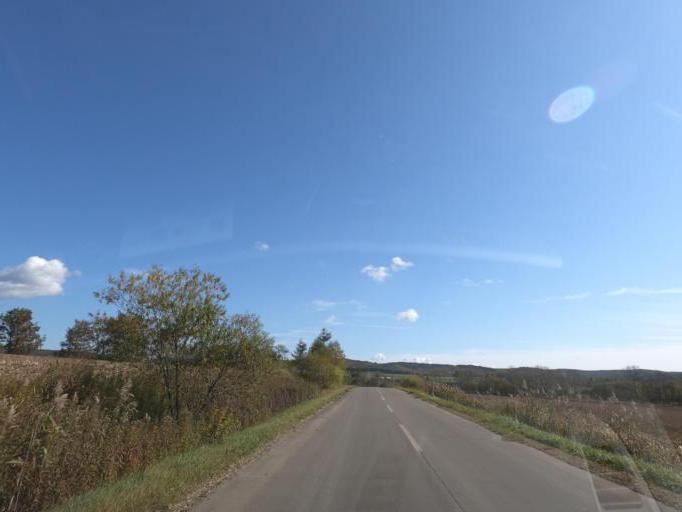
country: JP
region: Hokkaido
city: Otofuke
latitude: 43.0599
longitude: 143.2728
